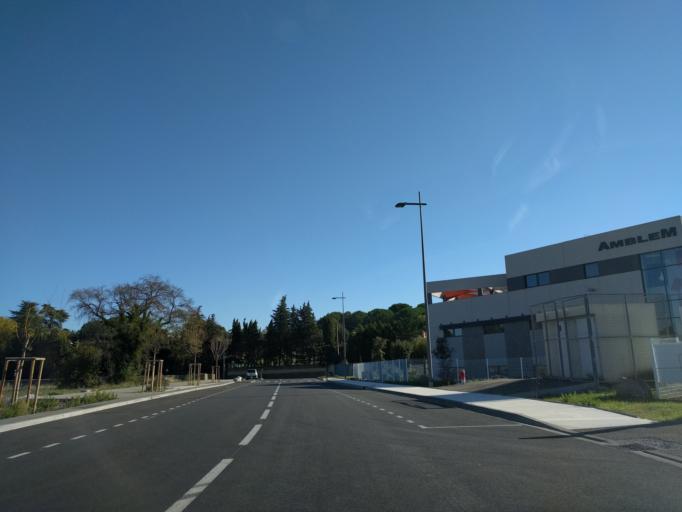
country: FR
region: Languedoc-Roussillon
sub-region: Departement de l'Herault
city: Castelnau-le-Lez
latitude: 43.6188
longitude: 3.9195
